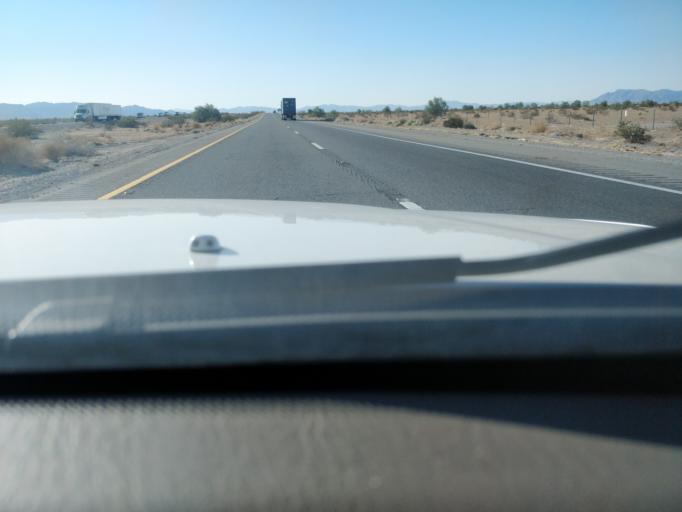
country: US
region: California
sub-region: Riverside County
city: Mesa Verde
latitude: 33.6500
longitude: -115.1336
